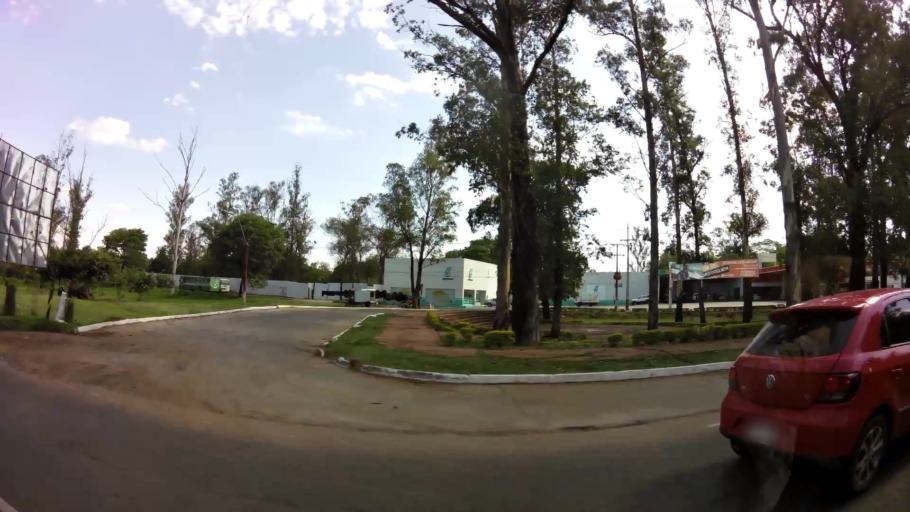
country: PY
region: Central
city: Fernando de la Mora
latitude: -25.3404
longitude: -57.5195
